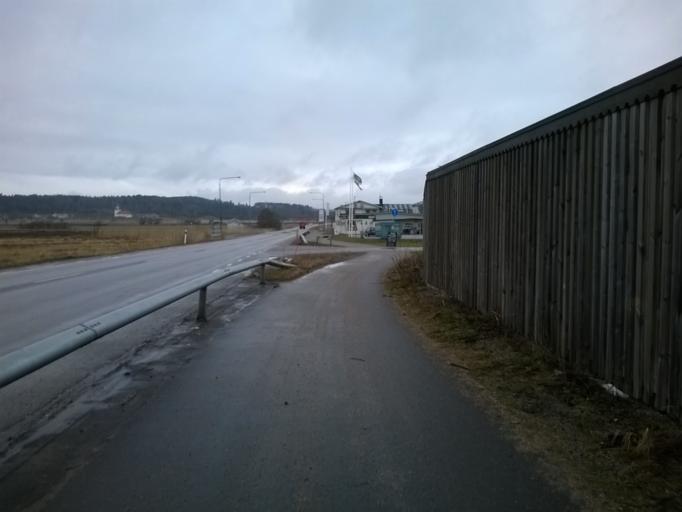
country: SE
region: Vaestra Goetaland
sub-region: Kungalvs Kommun
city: Kungalv
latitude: 57.9042
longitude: 11.9256
